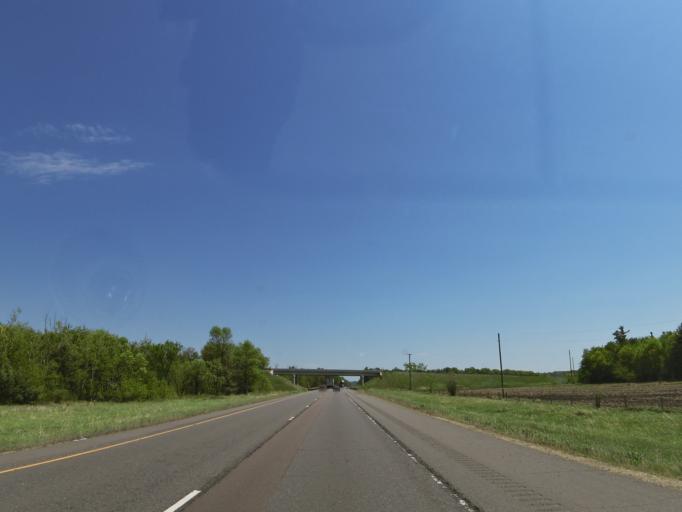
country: US
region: Wisconsin
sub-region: Monroe County
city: Tomah
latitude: 43.9542
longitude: -90.3498
